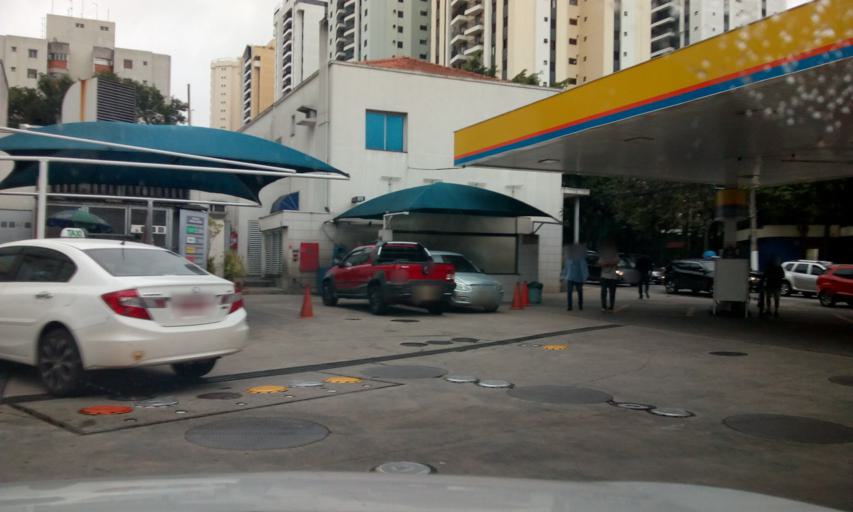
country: BR
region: Sao Paulo
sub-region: Sao Paulo
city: Sao Paulo
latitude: -23.6038
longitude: -46.6746
